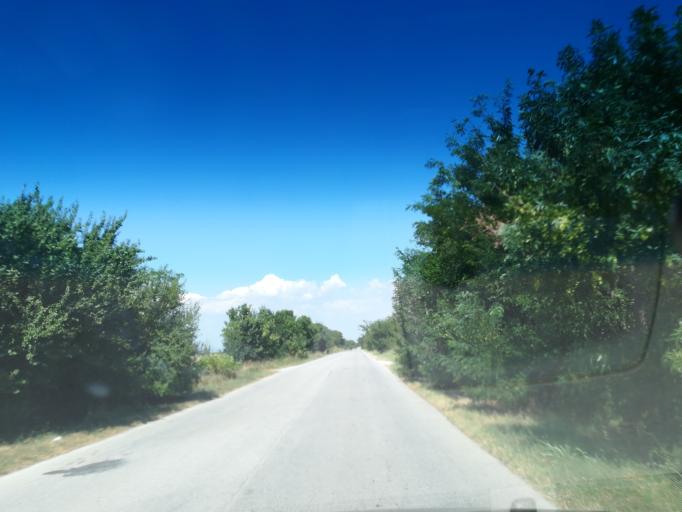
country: BG
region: Plovdiv
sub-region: Obshtina Sadovo
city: Sadovo
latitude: 42.0452
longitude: 25.1391
